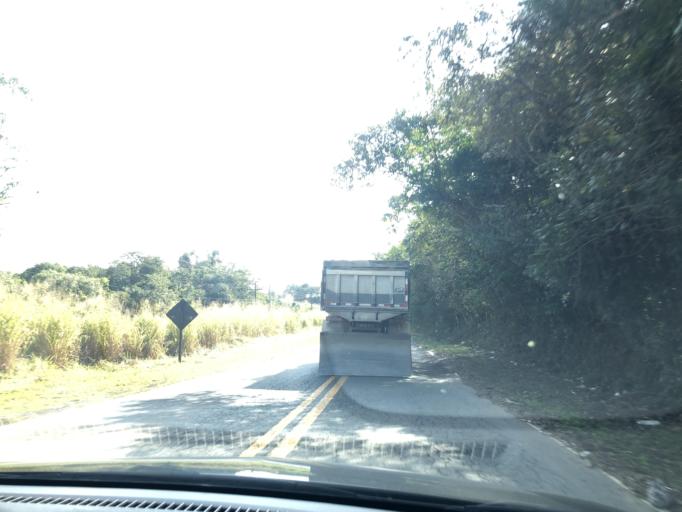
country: BR
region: Sao Paulo
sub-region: Pilar Do Sul
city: Pilar do Sul
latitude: -23.8090
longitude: -47.6958
